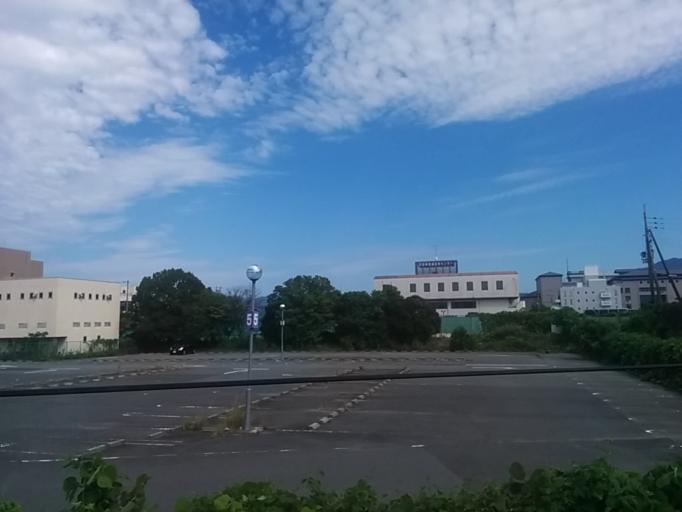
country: JP
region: Nara
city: Kashihara-shi
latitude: 34.5009
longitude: 135.7927
